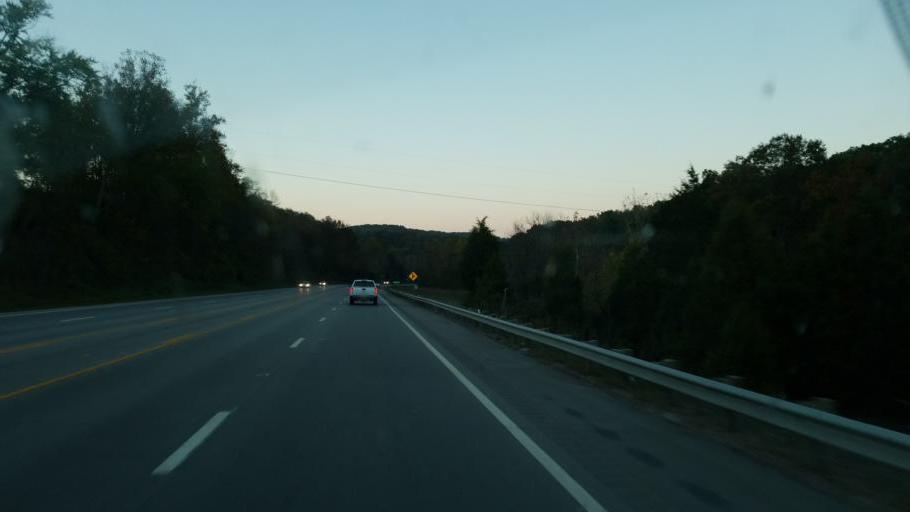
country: US
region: Ohio
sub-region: Pike County
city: Waverly
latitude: 39.1713
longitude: -82.9757
